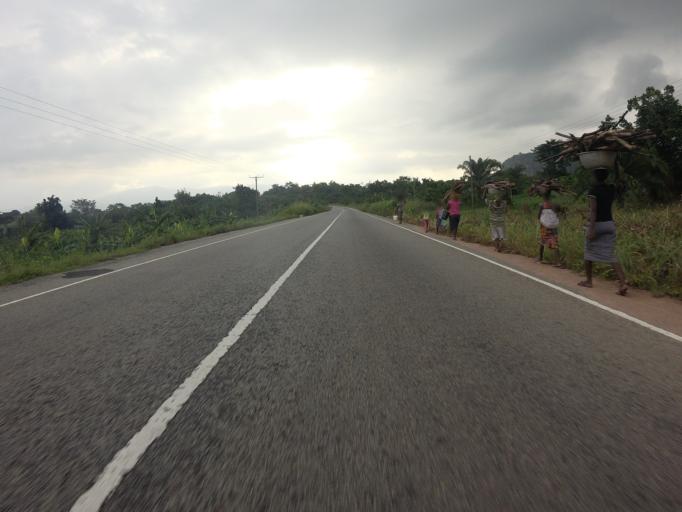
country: GH
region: Volta
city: Ho
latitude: 6.7855
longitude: 0.4554
